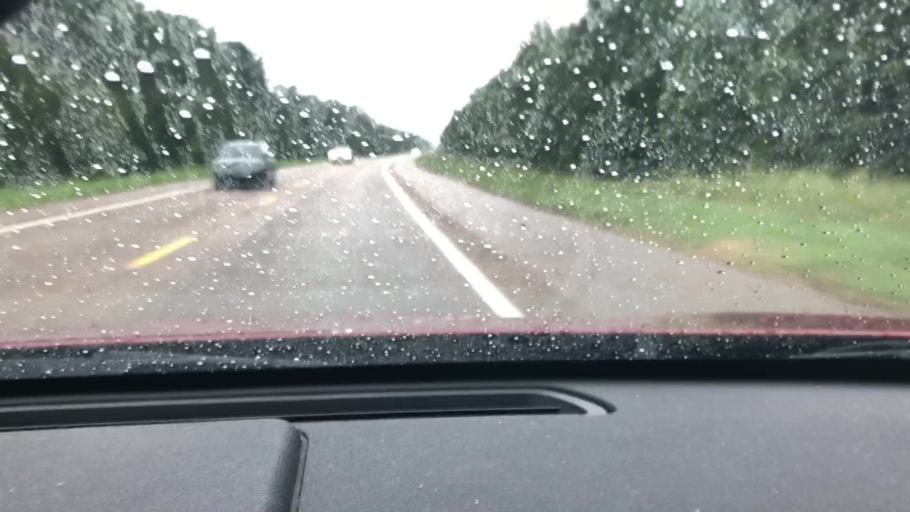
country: US
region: Arkansas
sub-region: Columbia County
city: Magnolia
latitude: 33.2991
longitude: -93.2642
